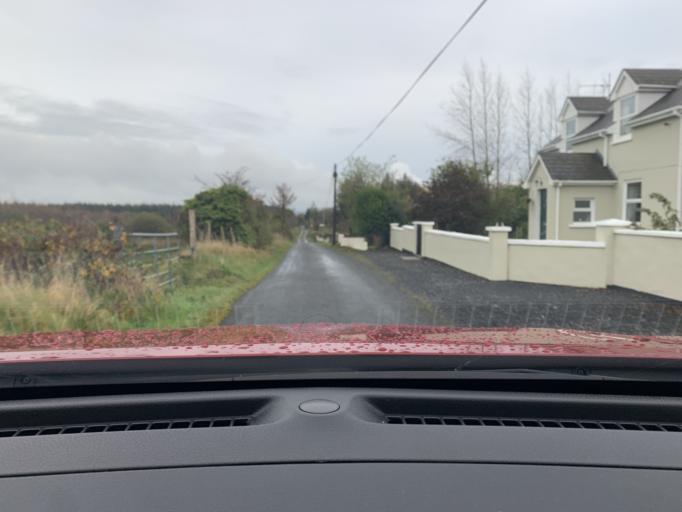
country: IE
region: Connaught
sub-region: Roscommon
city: Ballaghaderreen
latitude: 53.9224
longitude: -8.5613
